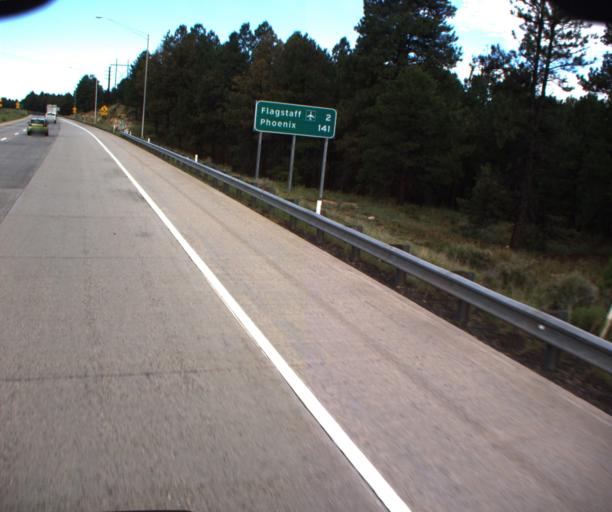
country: US
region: Arizona
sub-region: Coconino County
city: Flagstaff
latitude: 35.1623
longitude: -111.6749
